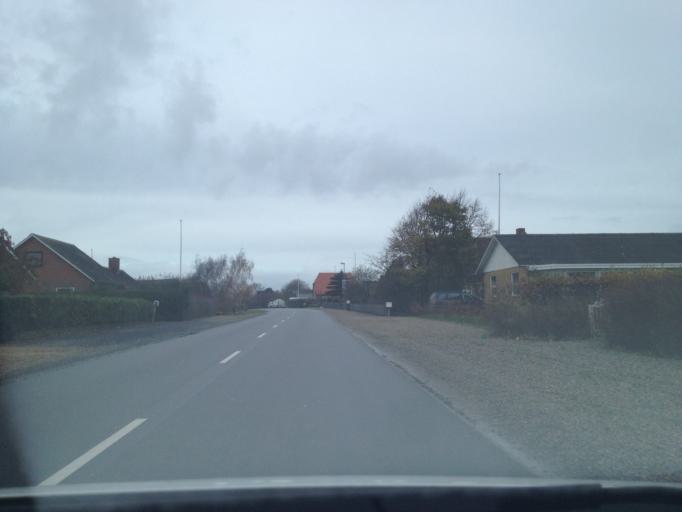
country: DK
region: South Denmark
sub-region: Esbjerg Kommune
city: Ribe
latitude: 55.2560
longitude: 8.8229
